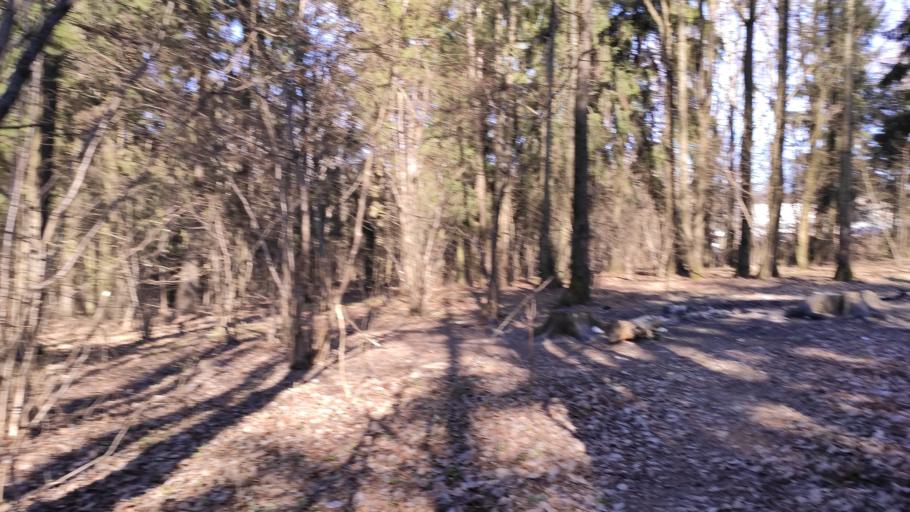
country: BY
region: Minsk
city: Novoye Medvezhino
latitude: 53.8879
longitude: 27.4544
